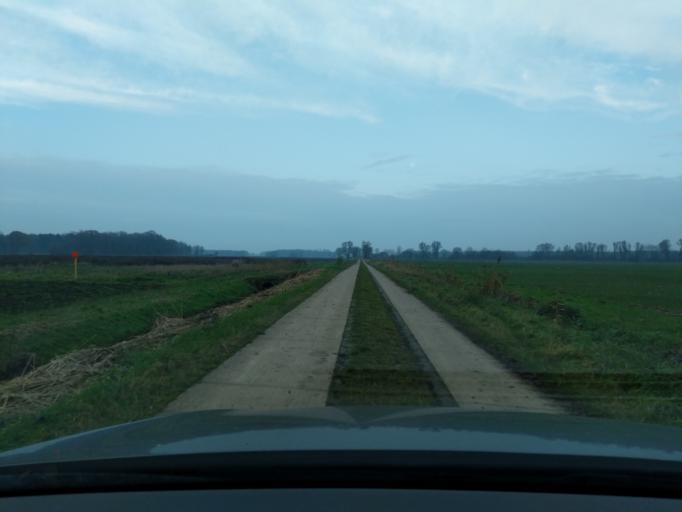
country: DE
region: Lower Saxony
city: Artlenburg
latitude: 53.3639
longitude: 10.4636
